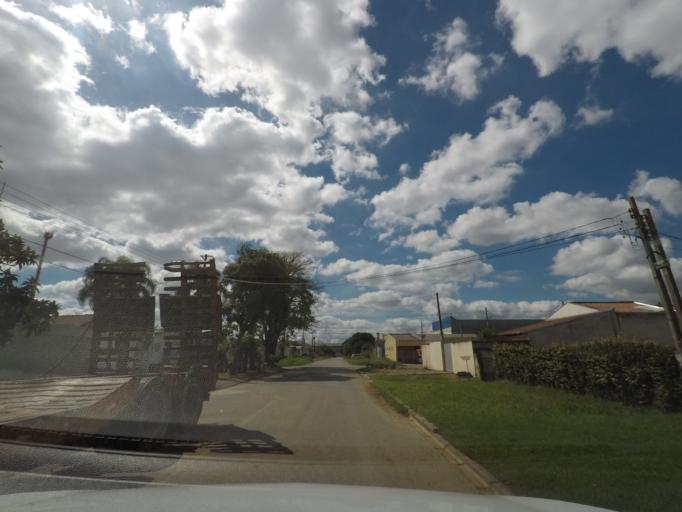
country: BR
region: Parana
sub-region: Sao Jose Dos Pinhais
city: Sao Jose dos Pinhais
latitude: -25.5046
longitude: -49.2156
